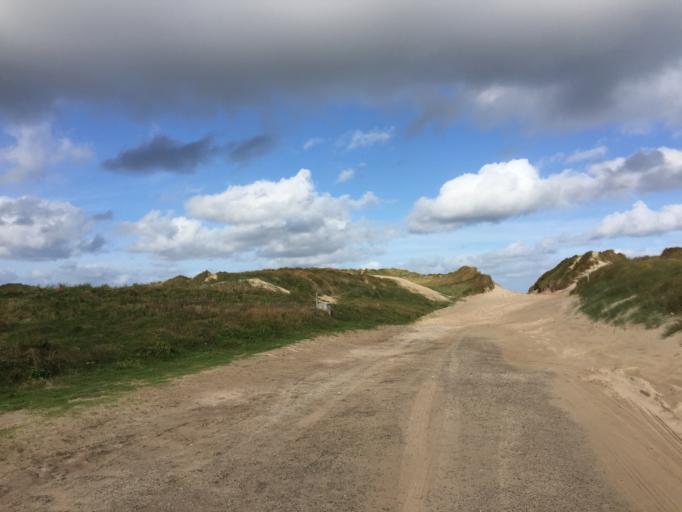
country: DK
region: North Denmark
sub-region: Thisted Kommune
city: Hanstholm
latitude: 57.0478
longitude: 8.5083
